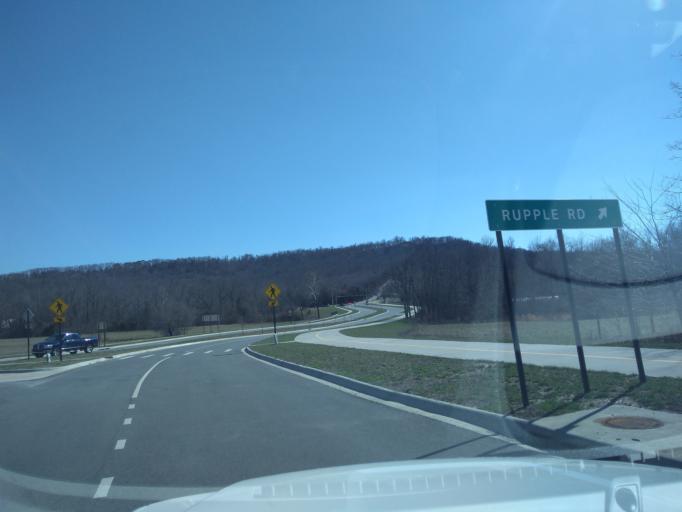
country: US
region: Arkansas
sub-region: Washington County
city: Farmington
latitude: 36.0513
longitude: -94.2203
